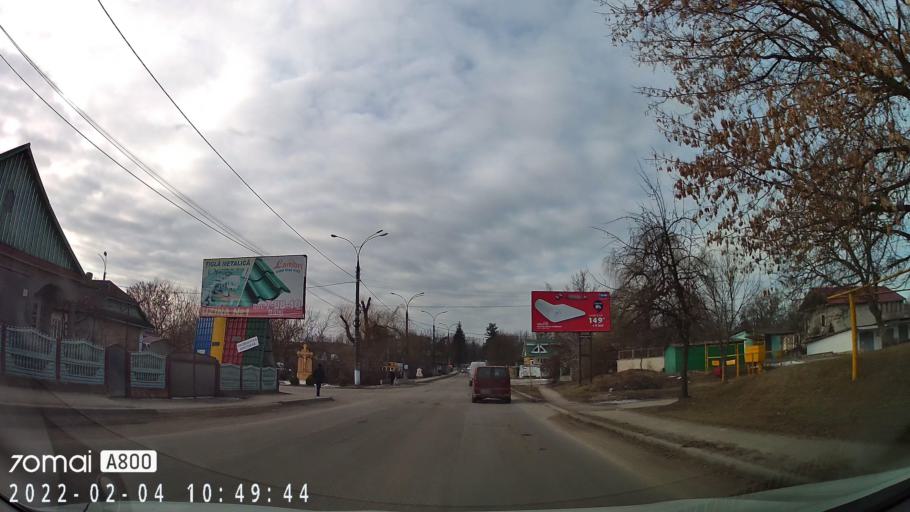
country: MD
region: Briceni
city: Briceni
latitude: 48.3573
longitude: 27.0897
